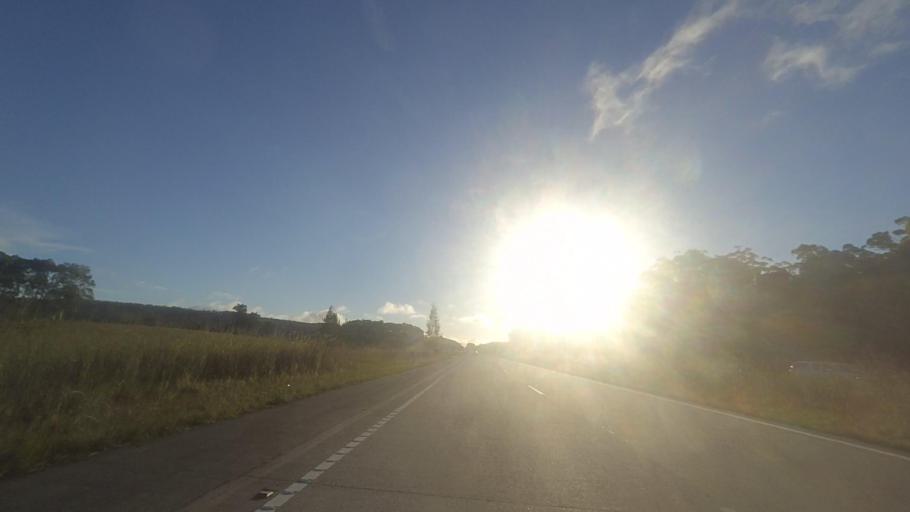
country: AU
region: New South Wales
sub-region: Great Lakes
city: Bulahdelah
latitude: -32.5241
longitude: 152.1977
